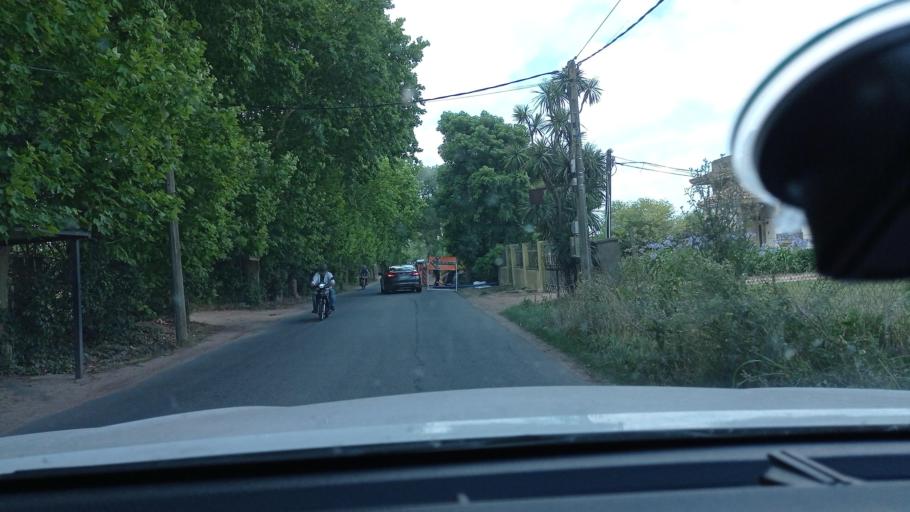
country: UY
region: Canelones
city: La Paz
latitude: -34.8146
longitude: -56.1947
